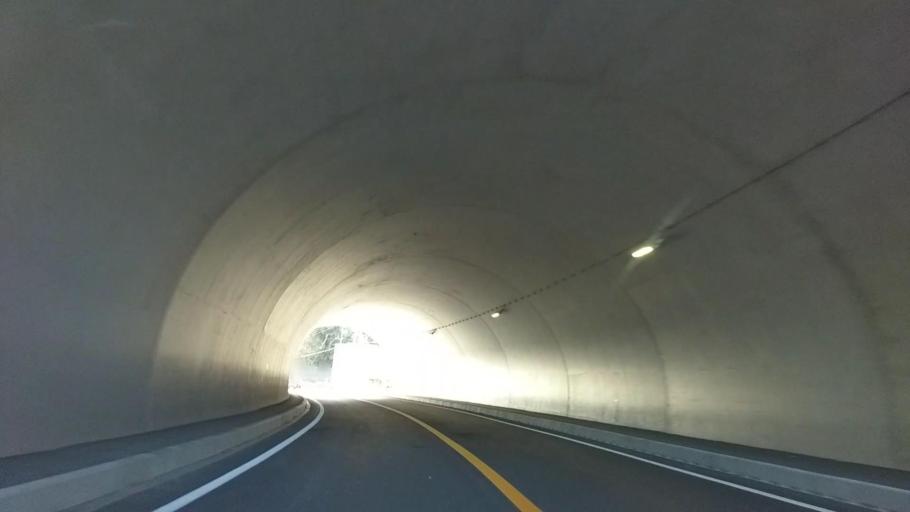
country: JP
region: Chiba
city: Tateyama
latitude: 35.0543
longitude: 139.8301
